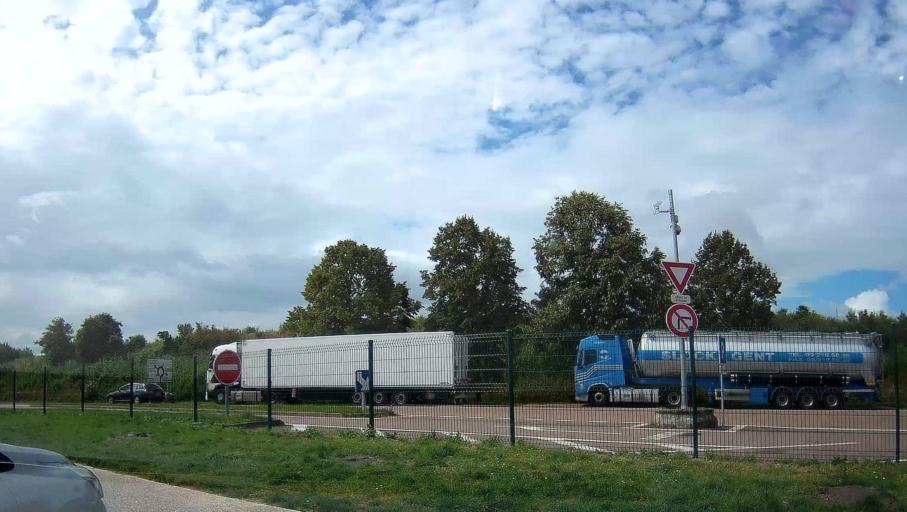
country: FR
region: Champagne-Ardenne
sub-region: Departement de l'Aube
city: Creney-pres-Troyes
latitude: 48.4101
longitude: 4.1432
